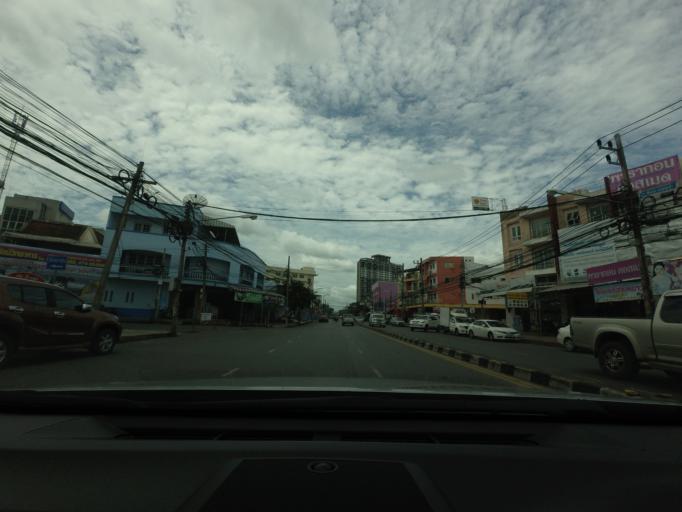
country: TH
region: Songkhla
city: Hat Yai
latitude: 7.0073
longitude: 100.4601
